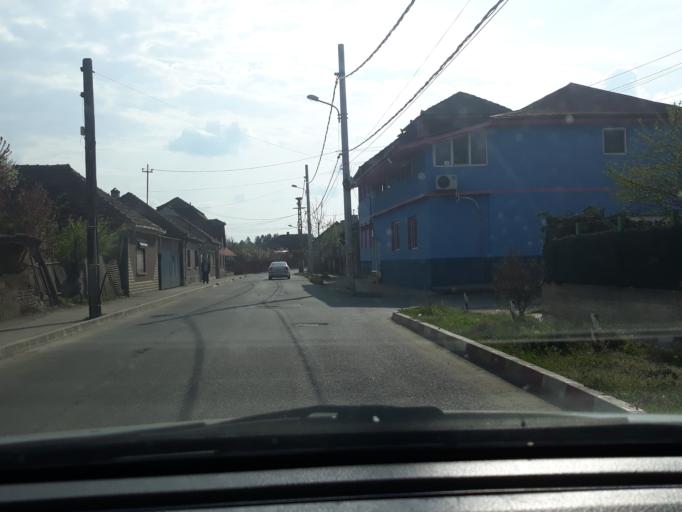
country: RO
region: Bihor
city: Margita
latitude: 47.3517
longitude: 22.3423
